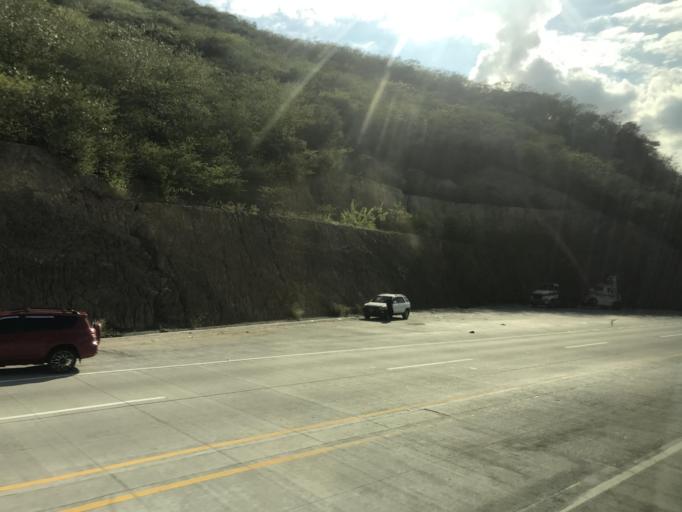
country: GT
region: El Progreso
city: Guastatoya
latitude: 14.8541
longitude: -90.0978
